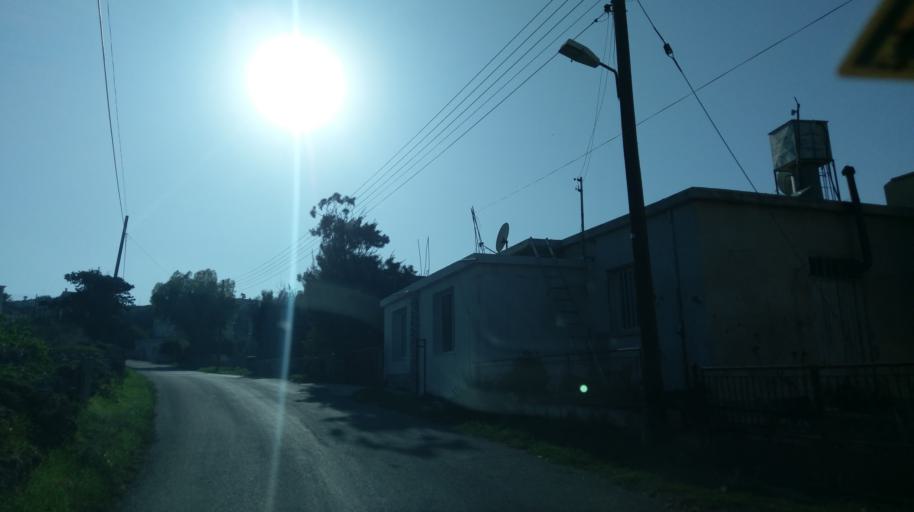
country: CY
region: Ammochostos
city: Leonarisso
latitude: 35.5392
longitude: 34.1914
